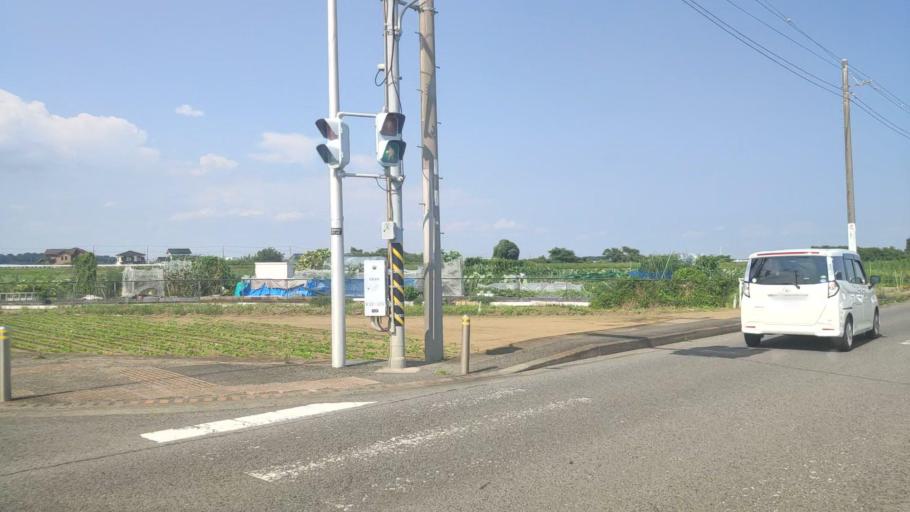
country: JP
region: Kanagawa
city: Isehara
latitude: 35.3650
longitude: 139.3168
